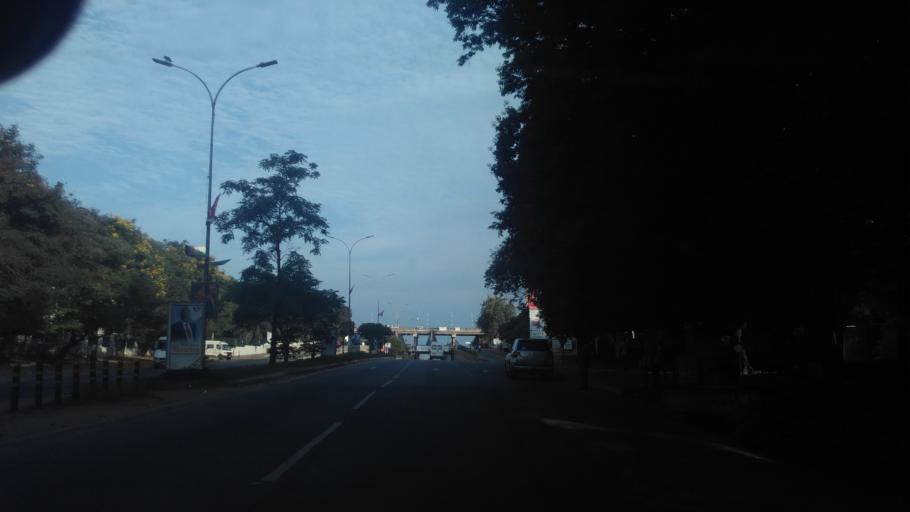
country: GH
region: Greater Accra
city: Accra
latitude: 5.5732
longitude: -0.1926
